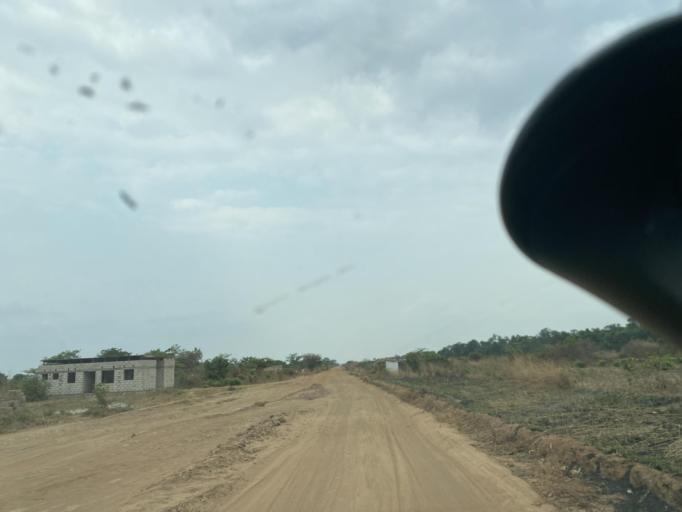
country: ZM
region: Lusaka
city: Lusaka
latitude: -15.2097
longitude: 28.3397
